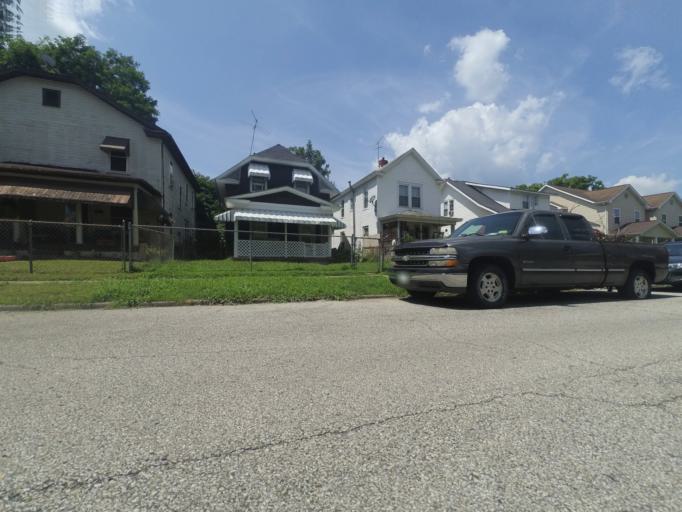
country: US
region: West Virginia
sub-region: Cabell County
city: Huntington
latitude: 38.4132
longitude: -82.4276
